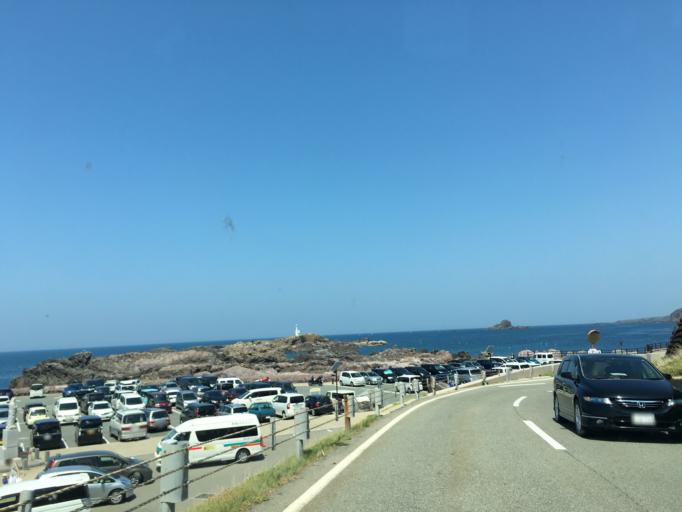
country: JP
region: Akita
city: Tenno
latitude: 39.9432
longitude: 139.7047
